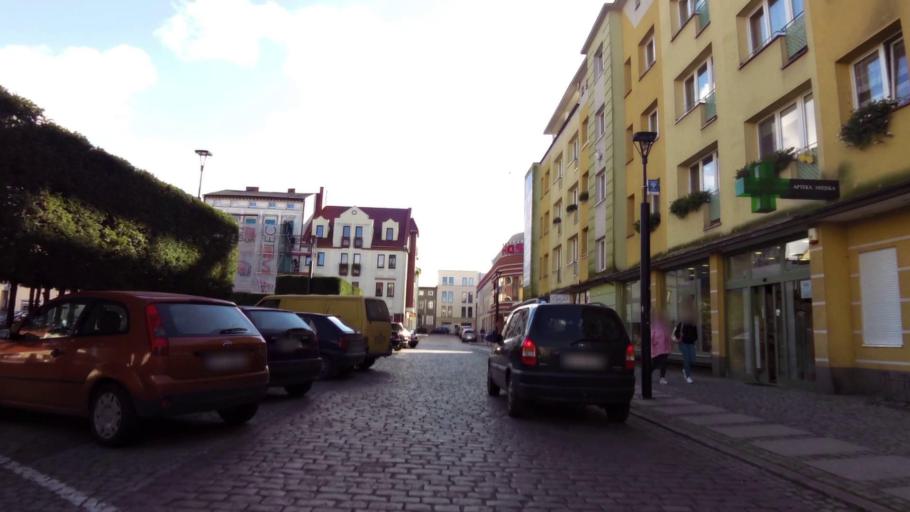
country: PL
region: West Pomeranian Voivodeship
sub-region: Powiat bialogardzki
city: Bialogard
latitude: 54.0047
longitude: 15.9898
